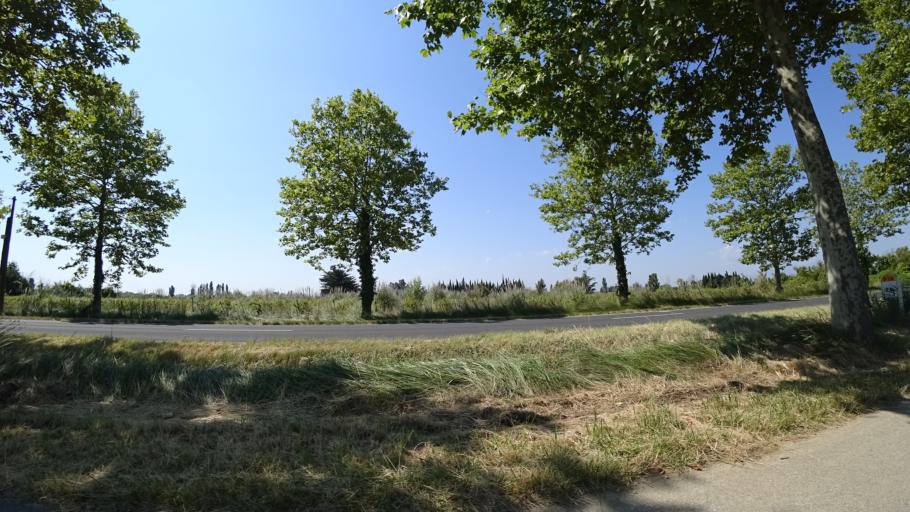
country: FR
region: Languedoc-Roussillon
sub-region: Departement des Pyrenees-Orientales
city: Villelongue-de-la-Salanque
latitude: 42.7272
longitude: 3.0027
